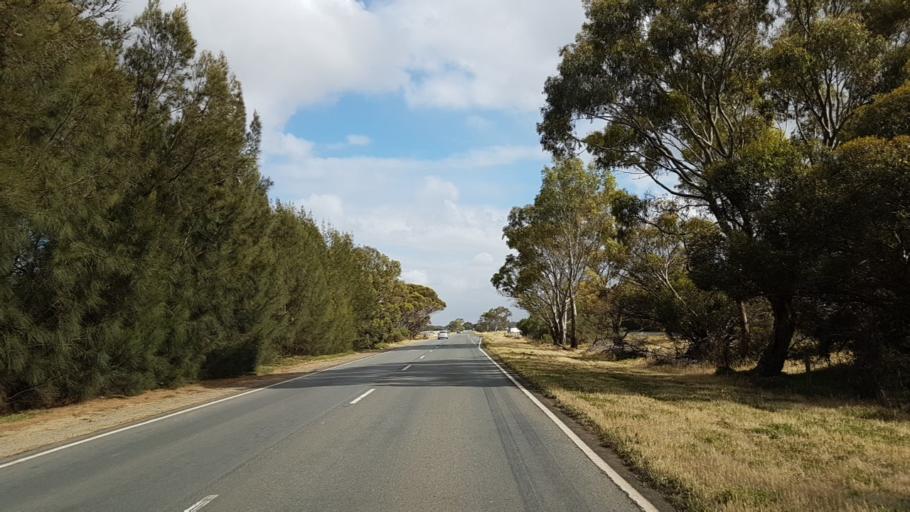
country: AU
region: South Australia
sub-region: Playford
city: Virginia
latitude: -34.6707
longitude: 138.5479
